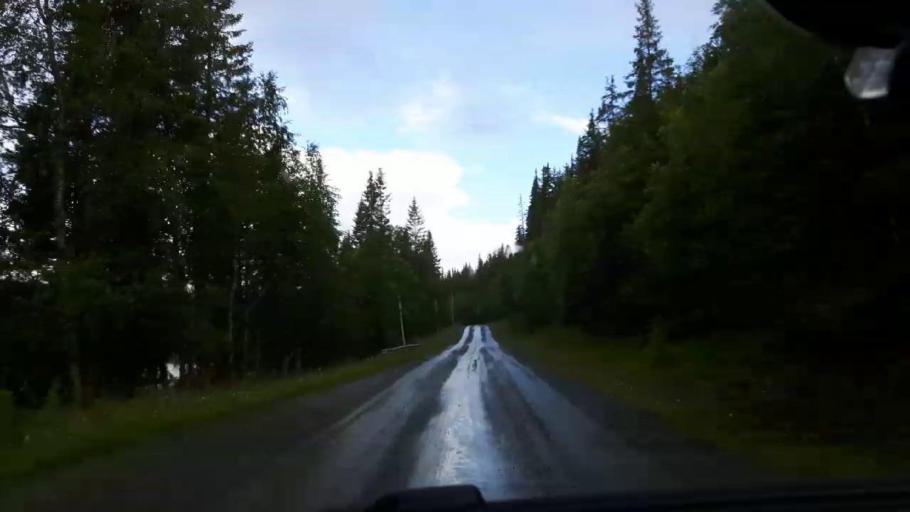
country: NO
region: Nordland
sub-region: Hattfjelldal
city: Hattfjelldal
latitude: 64.8643
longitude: 14.9044
